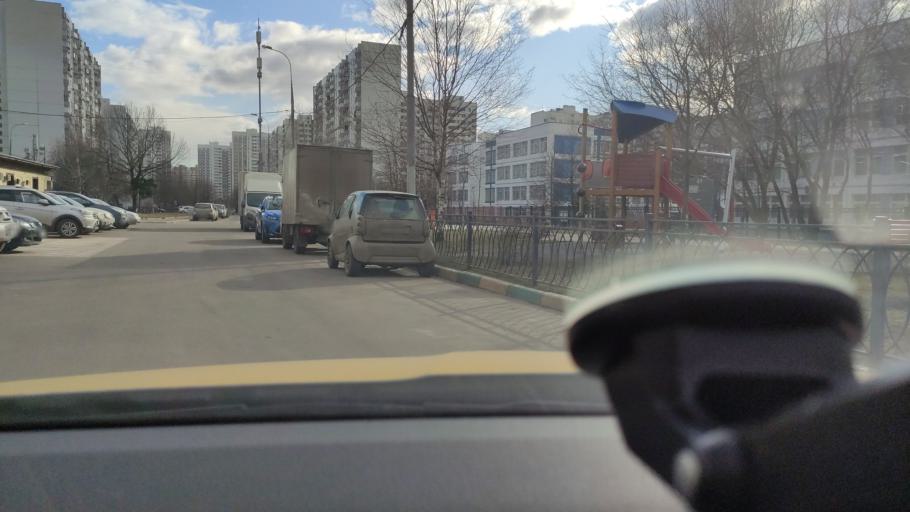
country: RU
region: Moskovskaya
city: Krasnogorsk
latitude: 55.8557
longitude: 37.3468
